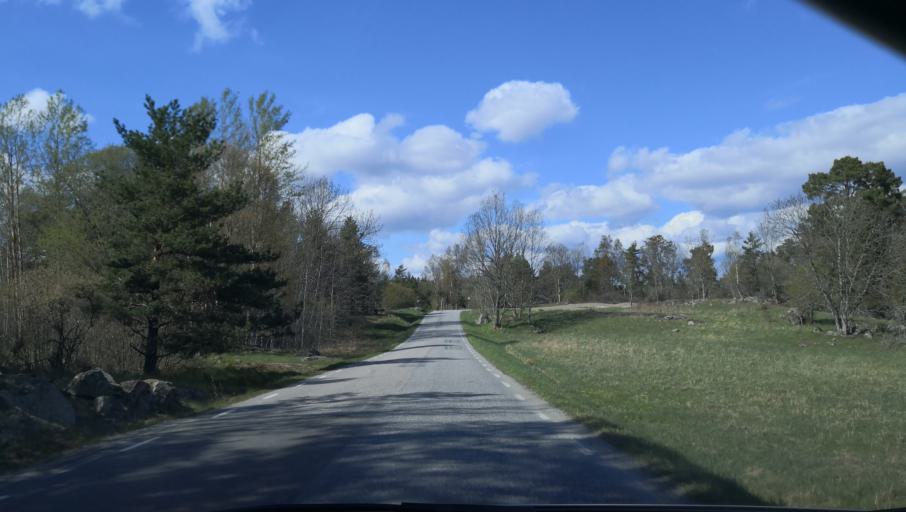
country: SE
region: Stockholm
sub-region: Varmdo Kommun
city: Hemmesta
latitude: 59.4052
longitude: 18.5056
